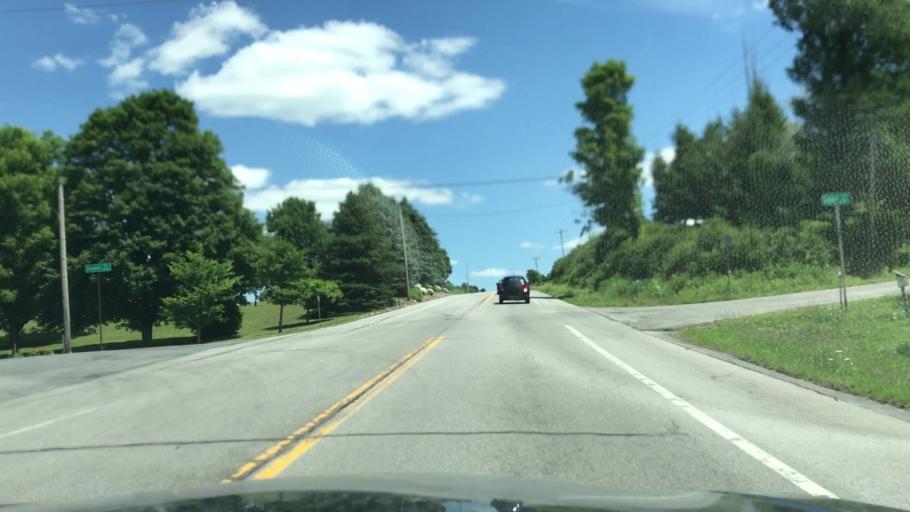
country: US
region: New York
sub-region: Wyoming County
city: Attica
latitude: 42.7559
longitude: -78.2787
